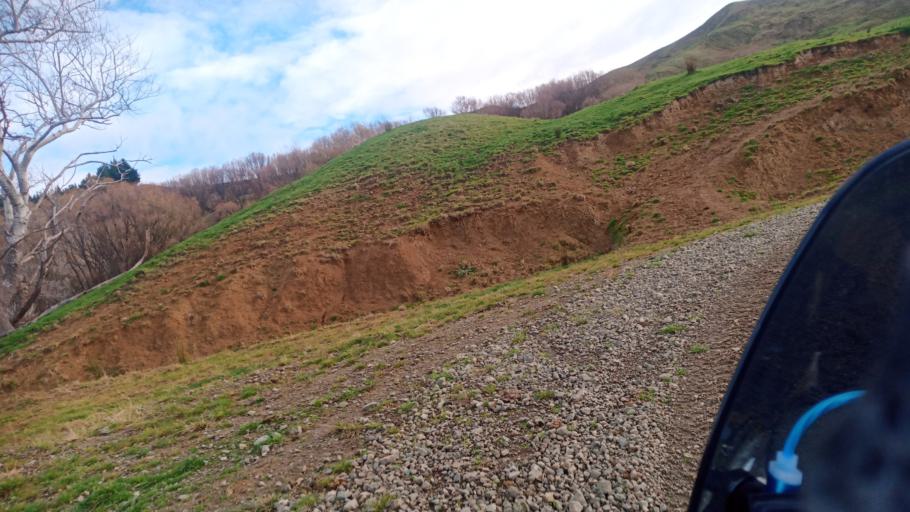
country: NZ
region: Gisborne
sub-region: Gisborne District
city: Gisborne
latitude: -38.3485
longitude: 177.9318
